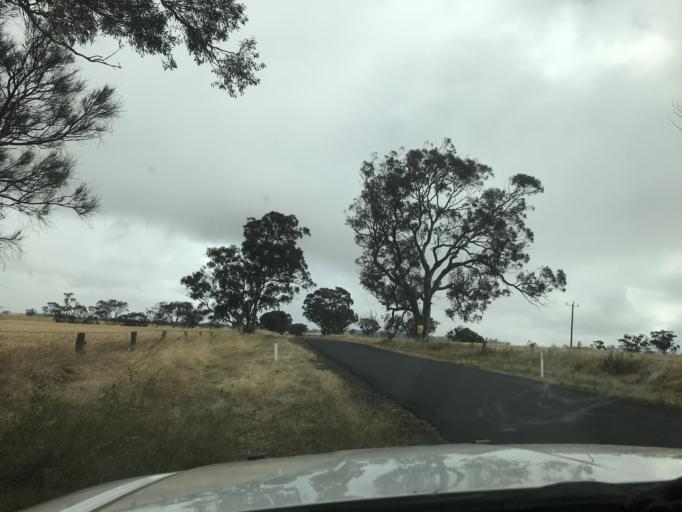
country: AU
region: South Australia
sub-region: Tatiara
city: Bordertown
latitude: -36.3321
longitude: 141.2987
